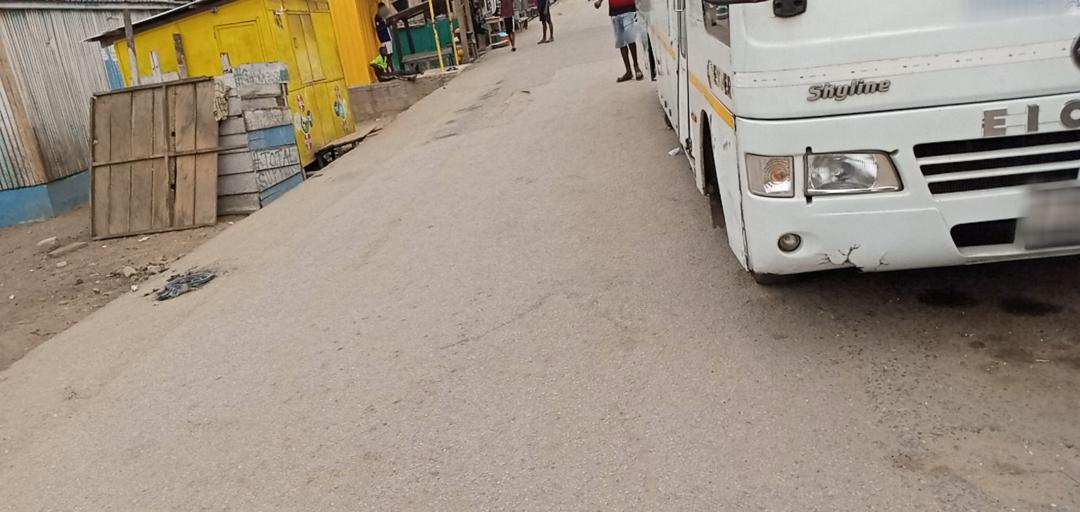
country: GH
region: Central
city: Winneba
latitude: 5.3449
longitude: -0.6209
